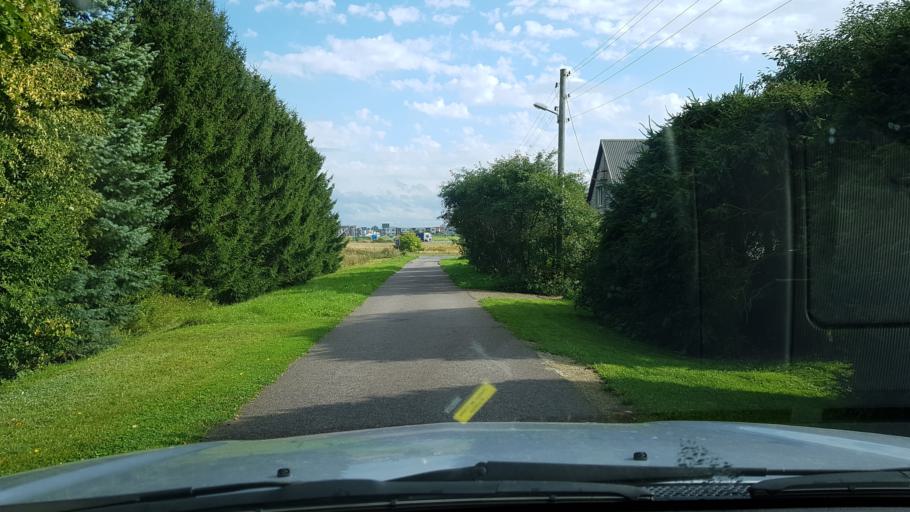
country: EE
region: Harju
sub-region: Rae vald
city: Jueri
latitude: 59.3572
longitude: 24.8806
